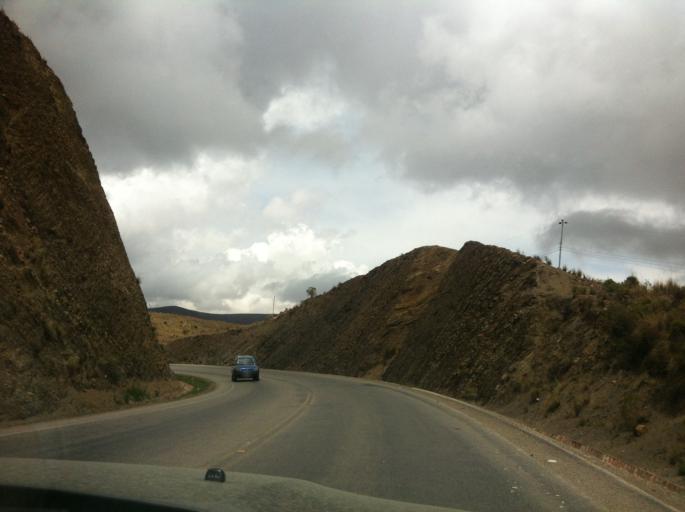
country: BO
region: Cochabamba
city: Irpa Irpa
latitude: -17.7090
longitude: -66.5283
